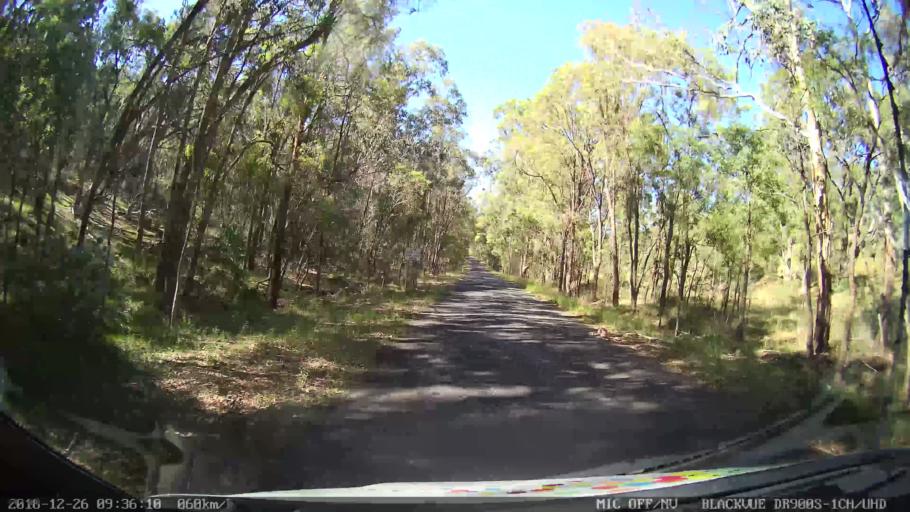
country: AU
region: New South Wales
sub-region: Mid-Western Regional
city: Kandos
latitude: -32.9216
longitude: 150.0405
